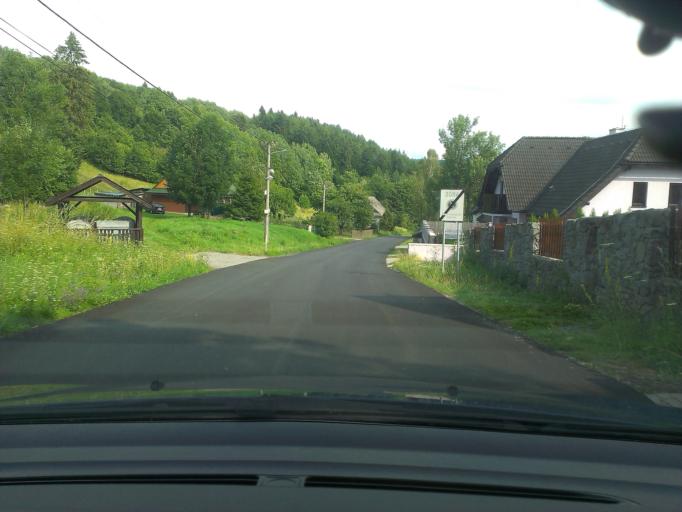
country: SK
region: Banskobystricky
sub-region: Okres Ziar nad Hronom
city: Kremnica
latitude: 48.7224
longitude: 18.9446
